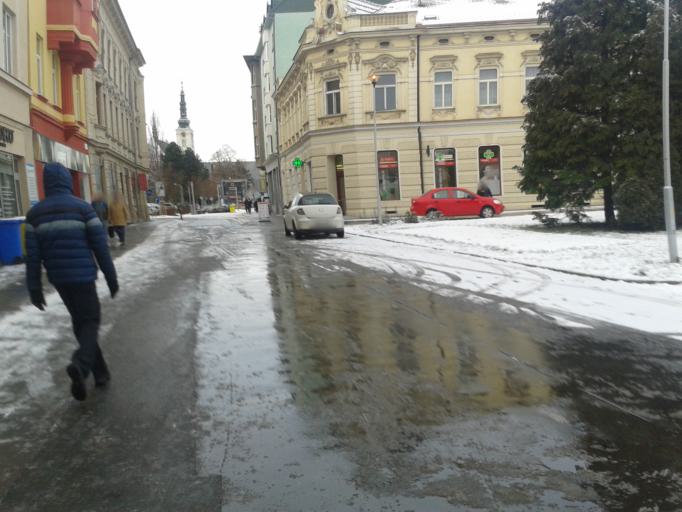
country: CZ
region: Olomoucky
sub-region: Okres Prostejov
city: Prostejov
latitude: 49.4728
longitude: 17.1166
